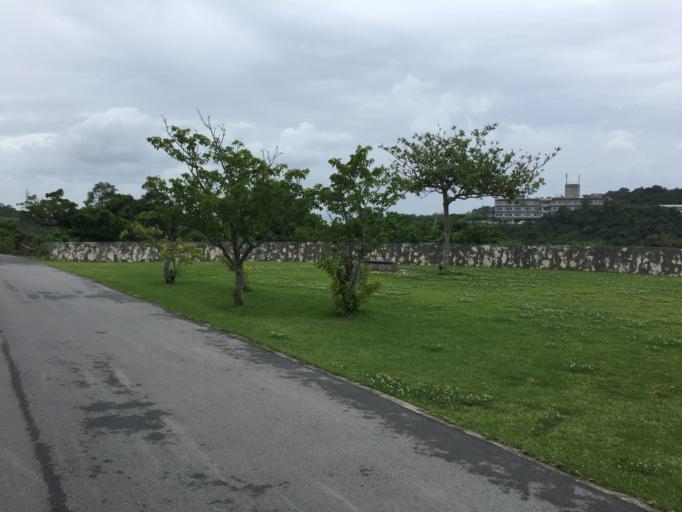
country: JP
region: Okinawa
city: Chatan
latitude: 26.2854
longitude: 127.8028
